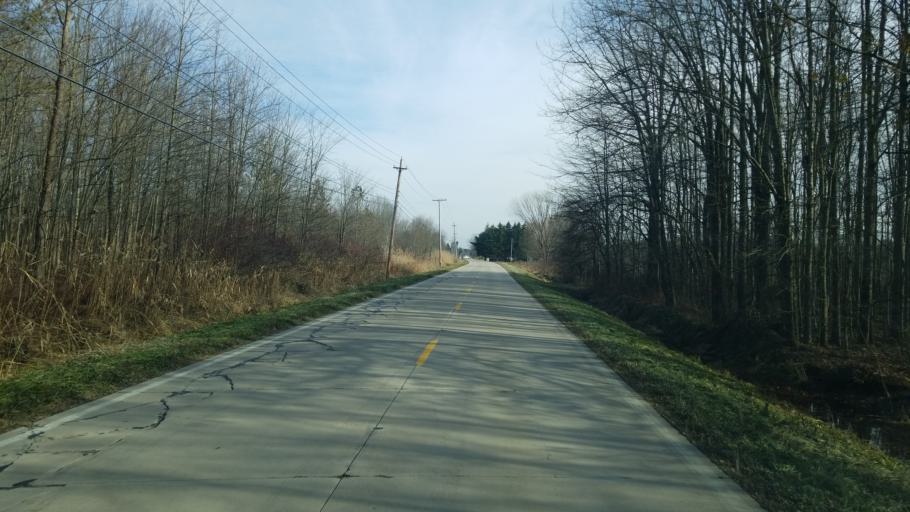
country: US
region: Ohio
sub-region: Ashtabula County
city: Roaming Shores
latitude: 41.6638
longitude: -80.9014
